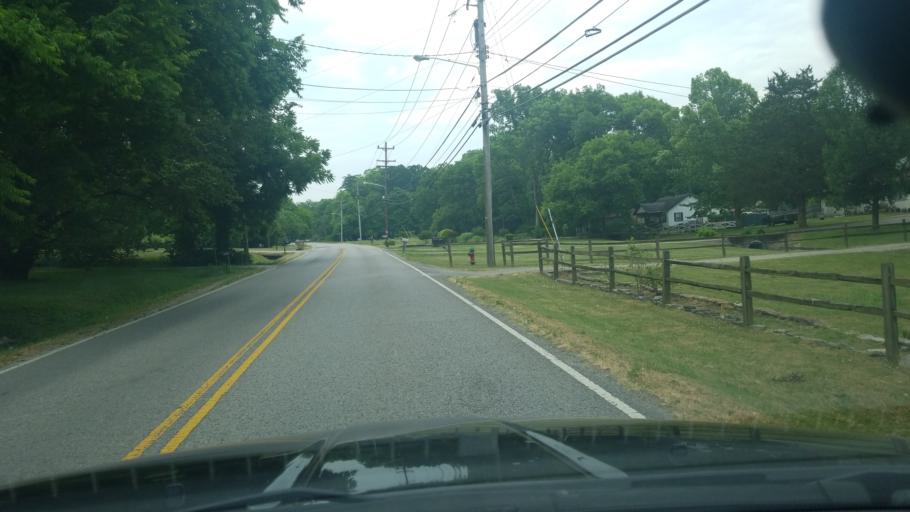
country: US
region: Tennessee
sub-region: Davidson County
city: Goodlettsville
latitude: 36.2553
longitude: -86.7528
